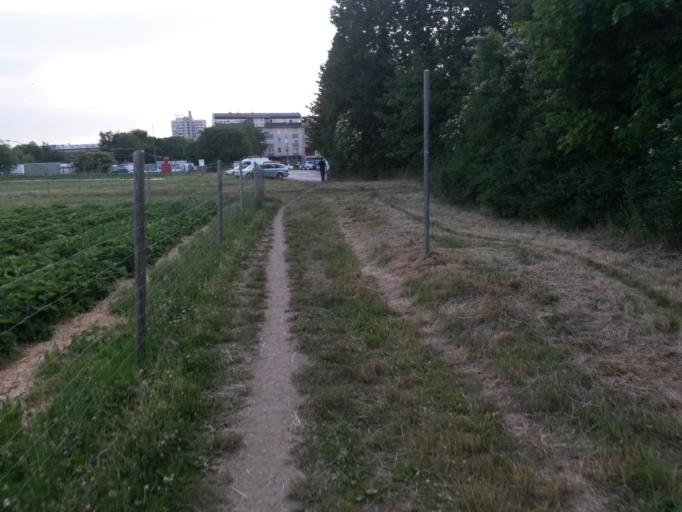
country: DE
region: Bavaria
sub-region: Upper Bavaria
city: Bogenhausen
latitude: 48.1111
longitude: 11.6199
